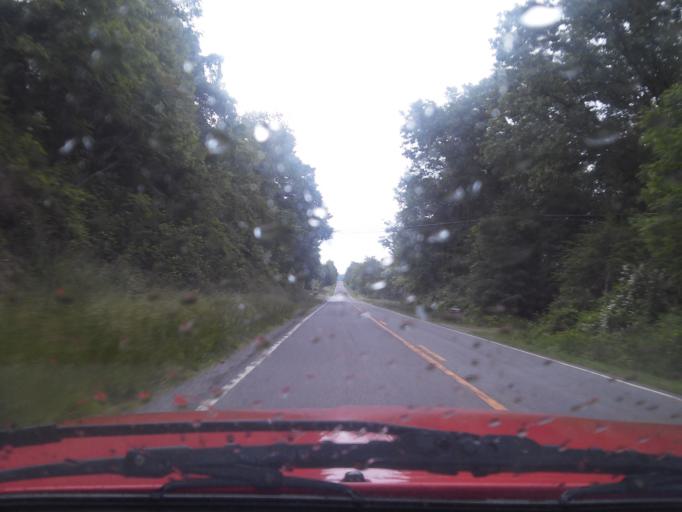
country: US
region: Virginia
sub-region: Montgomery County
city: Blacksburg
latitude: 37.3336
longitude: -80.4321
